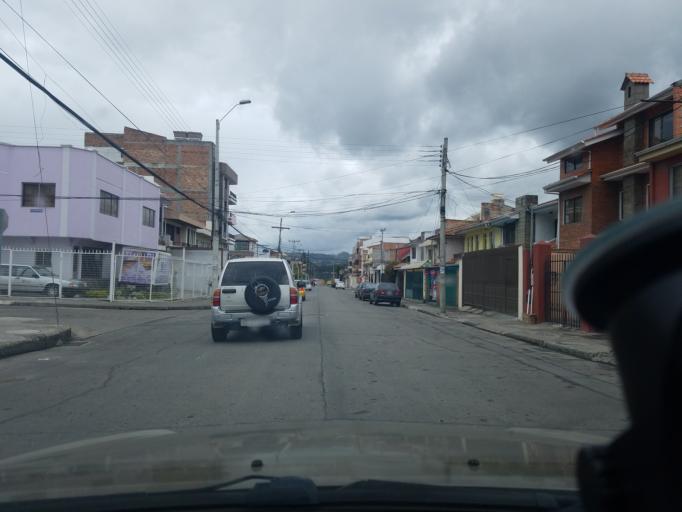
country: EC
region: Azuay
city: Cuenca
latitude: -2.9006
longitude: -78.9934
